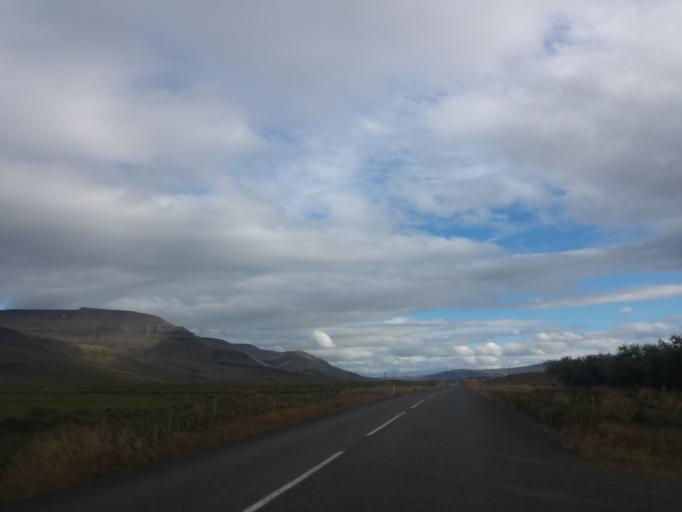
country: IS
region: West
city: Borgarnes
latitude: 64.4198
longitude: -21.8066
